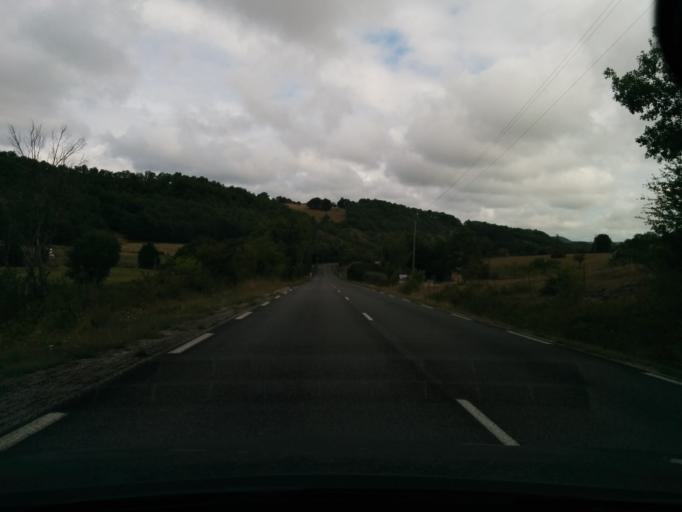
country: FR
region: Midi-Pyrenees
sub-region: Departement du Lot
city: Le Vigan
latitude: 44.6508
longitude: 1.4788
